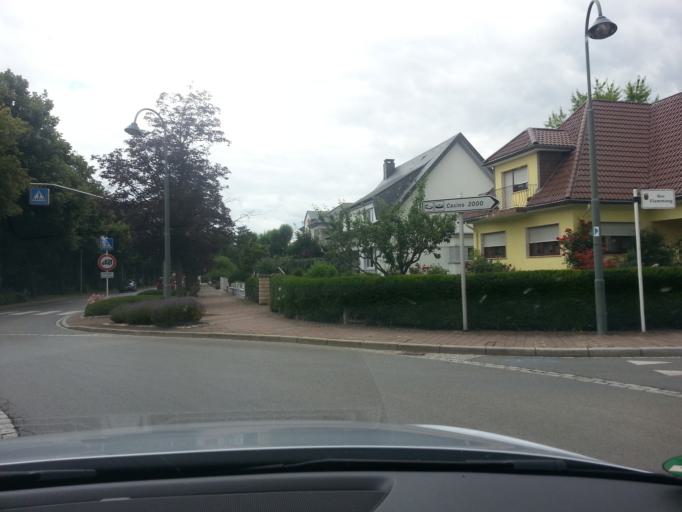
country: LU
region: Grevenmacher
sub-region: Canton de Remich
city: Mondorf-les-Bains
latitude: 49.5076
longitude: 6.2832
